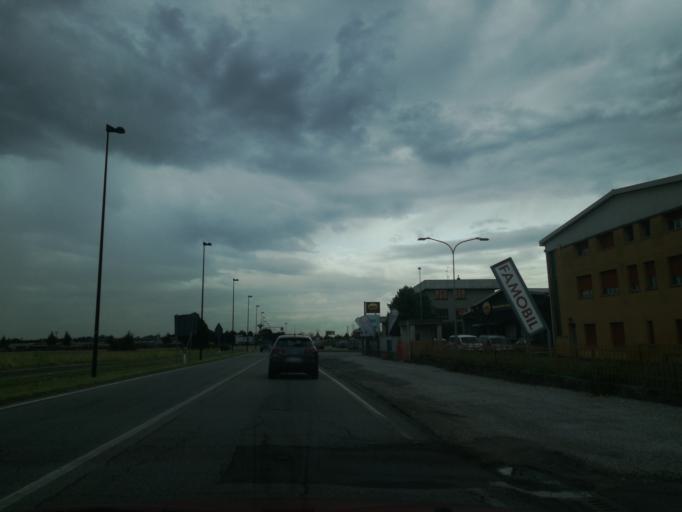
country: IT
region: Lombardy
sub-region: Provincia di Monza e Brianza
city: Bellusco
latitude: 45.6120
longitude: 9.4189
